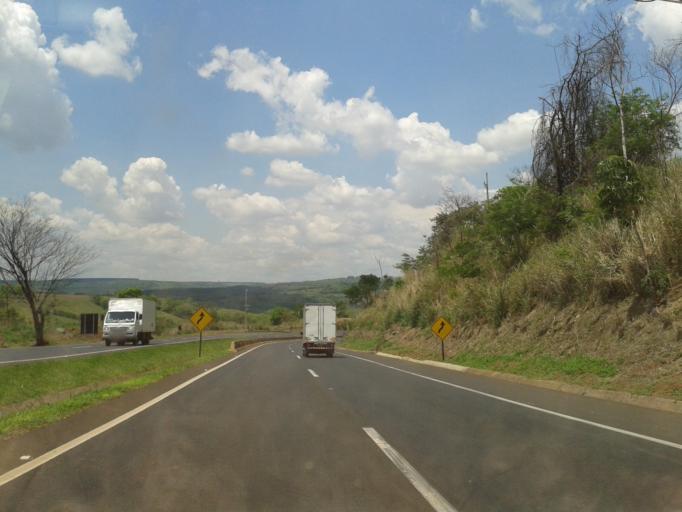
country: BR
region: Minas Gerais
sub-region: Araguari
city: Araguari
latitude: -18.7604
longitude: -48.2407
